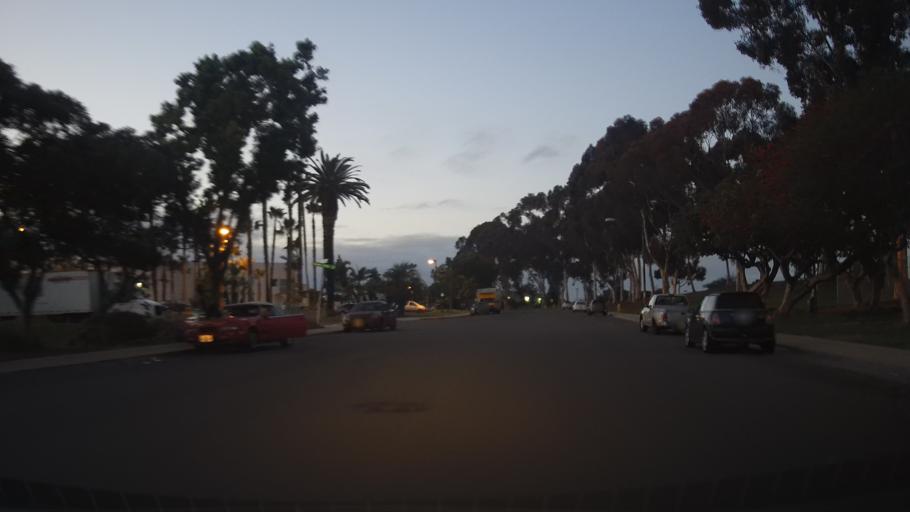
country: US
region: California
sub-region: San Diego County
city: National City
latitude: 32.7127
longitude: -117.1123
